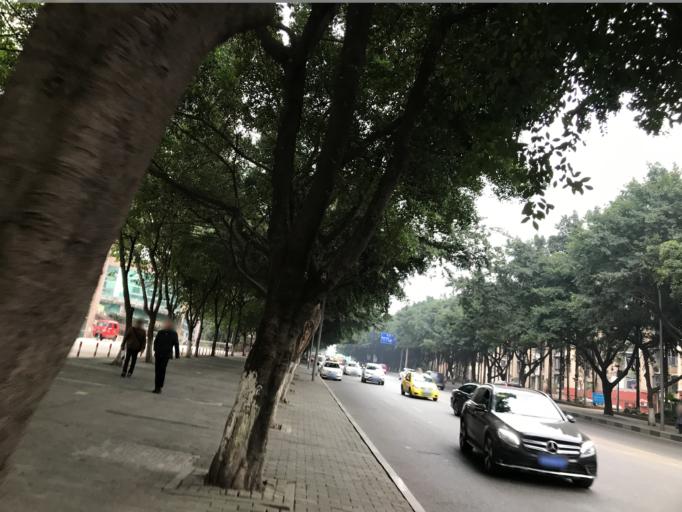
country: CN
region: Chongqing Shi
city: Chongqing
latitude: 29.5292
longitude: 106.5519
